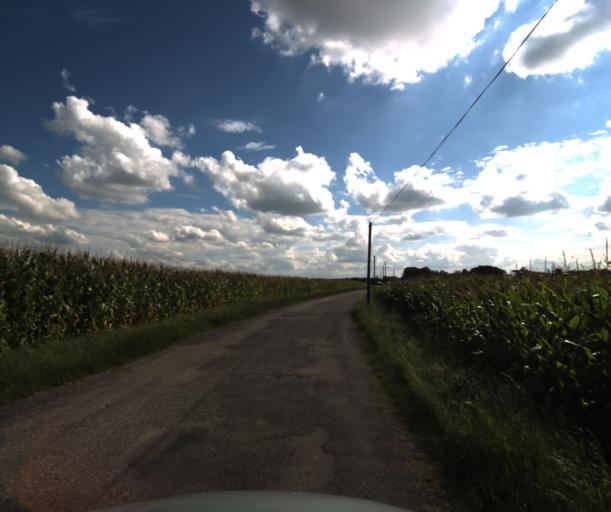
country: FR
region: Midi-Pyrenees
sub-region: Departement de la Haute-Garonne
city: Roquettes
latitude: 43.4825
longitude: 1.3689
